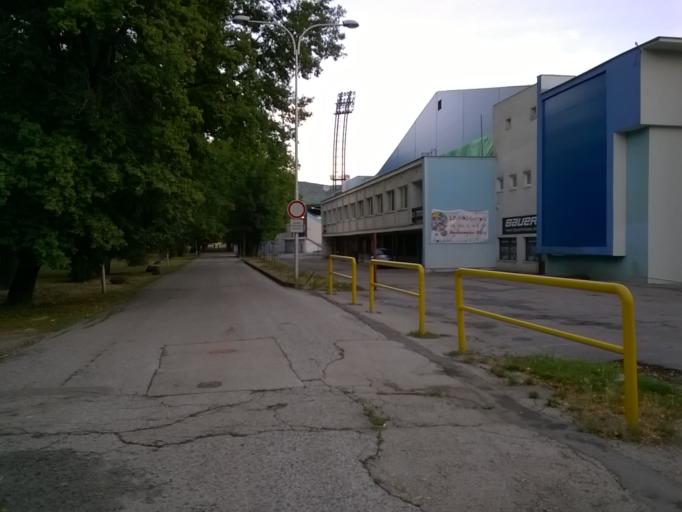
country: SK
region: Nitriansky
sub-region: Okres Nitra
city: Nitra
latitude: 48.3201
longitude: 18.0861
